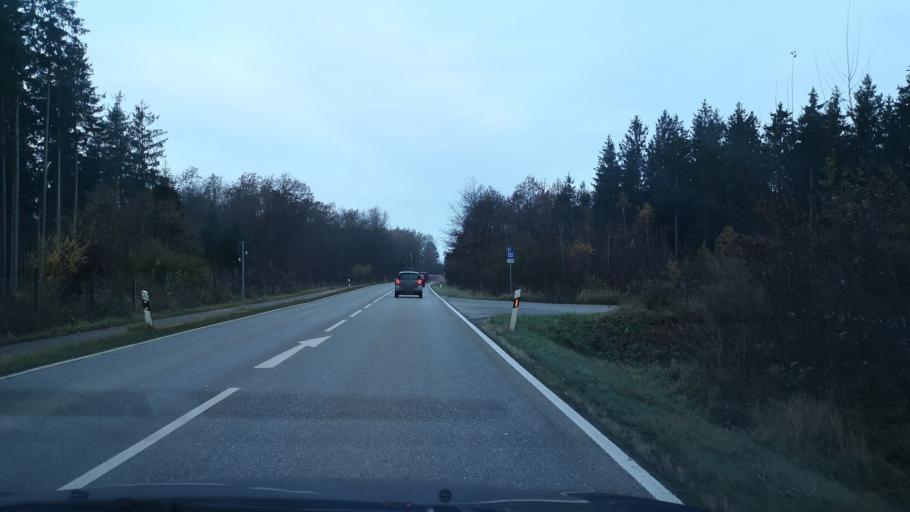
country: DE
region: Bavaria
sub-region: Upper Bavaria
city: Forstinning
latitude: 48.1542
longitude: 11.9074
